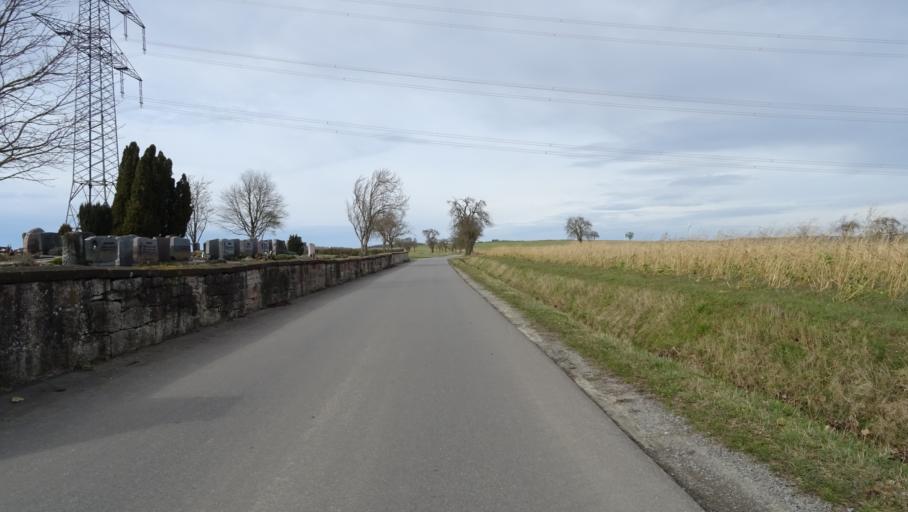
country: DE
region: Baden-Wuerttemberg
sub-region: Karlsruhe Region
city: Seckach
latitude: 49.4210
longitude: 9.2795
